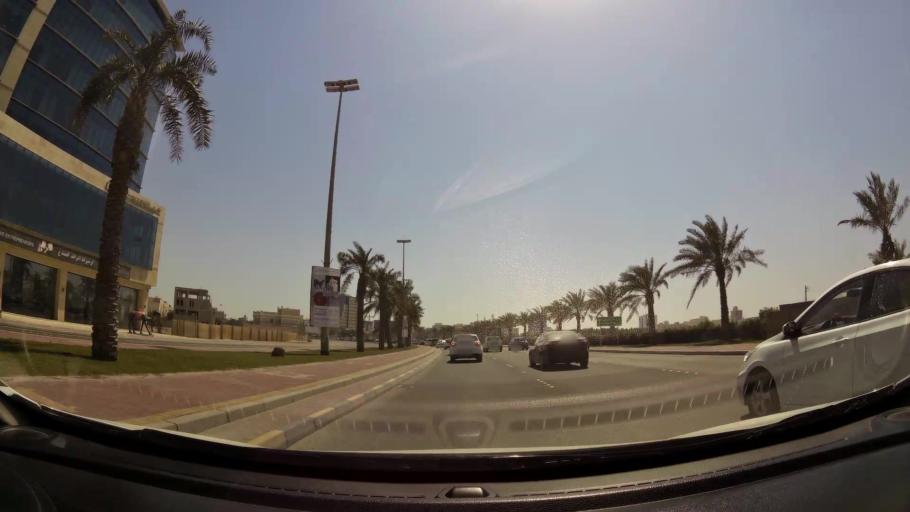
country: BH
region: Manama
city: Manama
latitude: 26.2117
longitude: 50.5968
